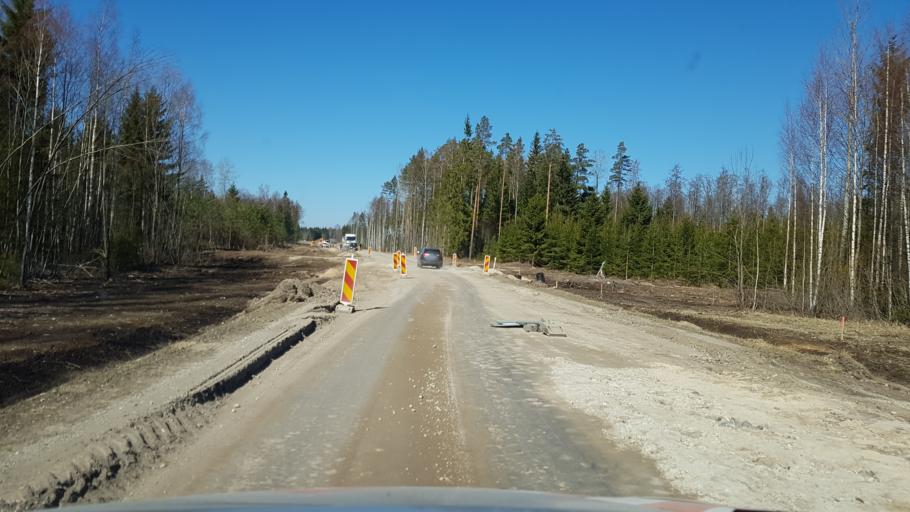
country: EE
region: Jogevamaa
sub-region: Mustvee linn
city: Mustvee
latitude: 59.0374
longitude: 26.6789
